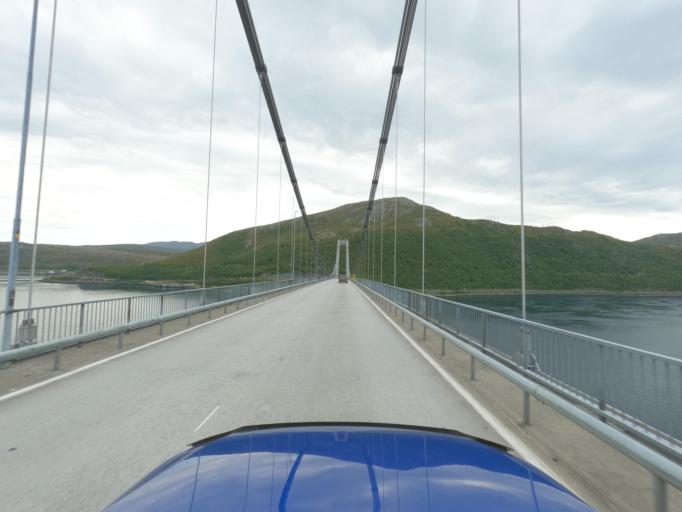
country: NO
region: Finnmark Fylke
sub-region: Kvalsund
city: Kvalsund
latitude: 70.5138
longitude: 23.9500
